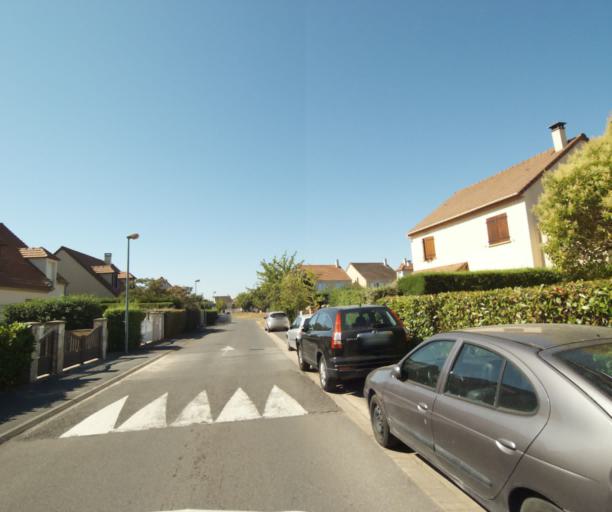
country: FR
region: Ile-de-France
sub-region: Departement de l'Essonne
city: Itteville
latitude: 48.5289
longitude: 2.3487
